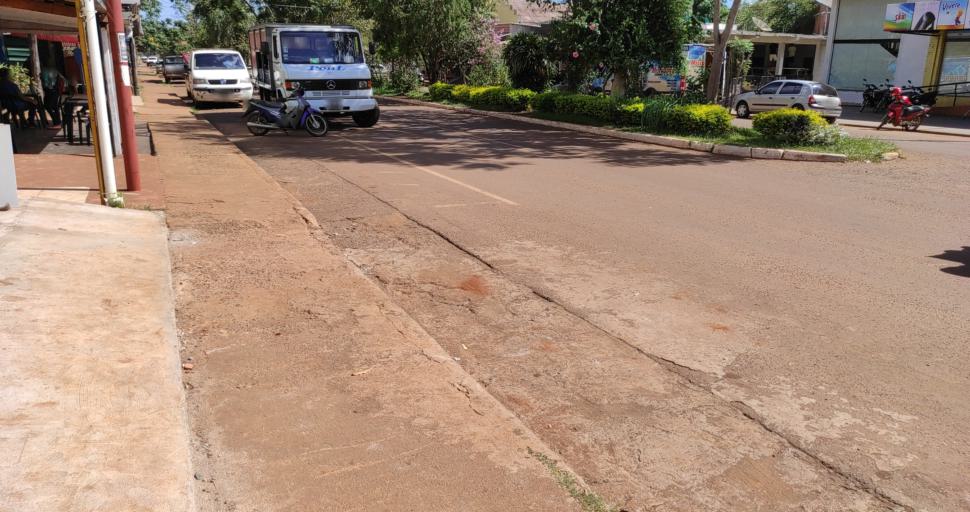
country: AR
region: Misiones
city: El Soberbio
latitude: -27.2949
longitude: -54.1981
